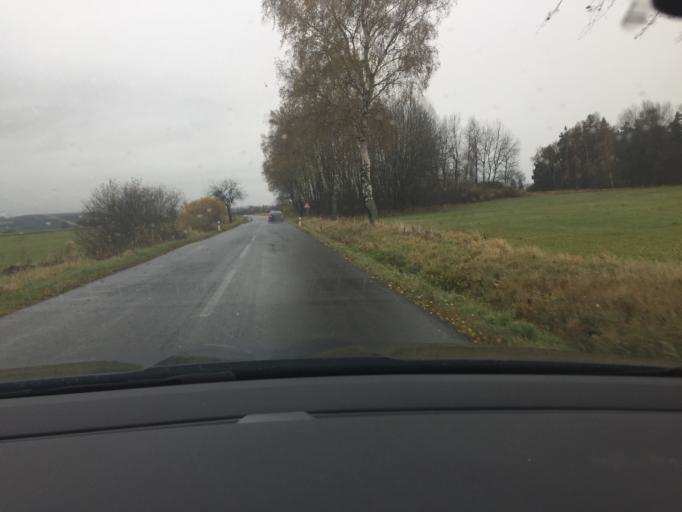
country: SK
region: Presovsky
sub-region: Okres Presov
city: Kezmarok
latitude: 49.1757
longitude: 20.4034
